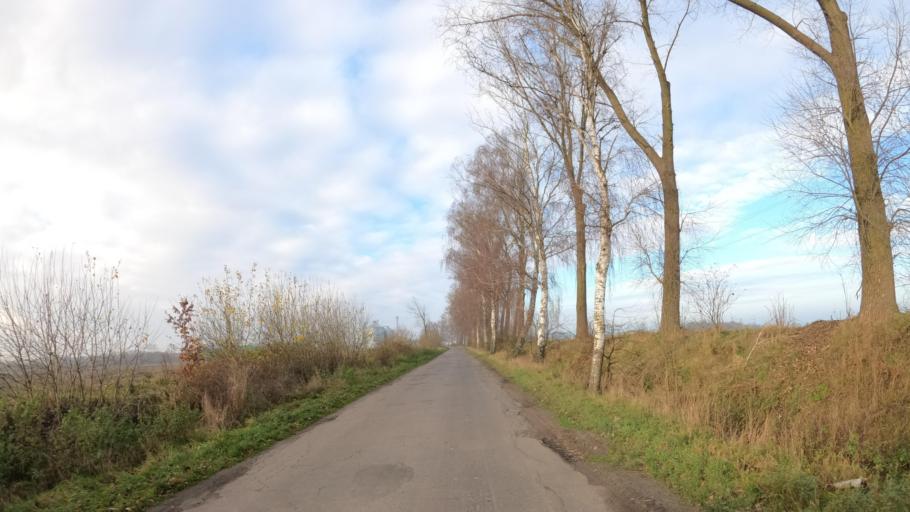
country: PL
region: West Pomeranian Voivodeship
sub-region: Powiat goleniowski
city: Osina
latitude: 53.5775
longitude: 15.0890
